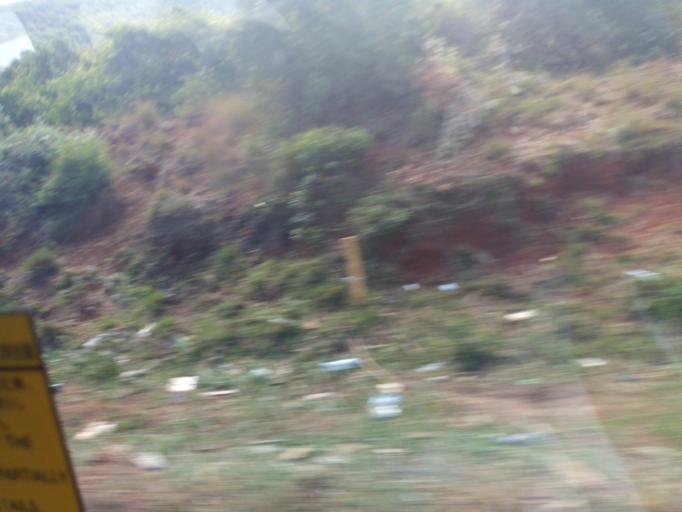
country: KE
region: Nakuru
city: Kijabe
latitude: -1.0161
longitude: 36.6010
